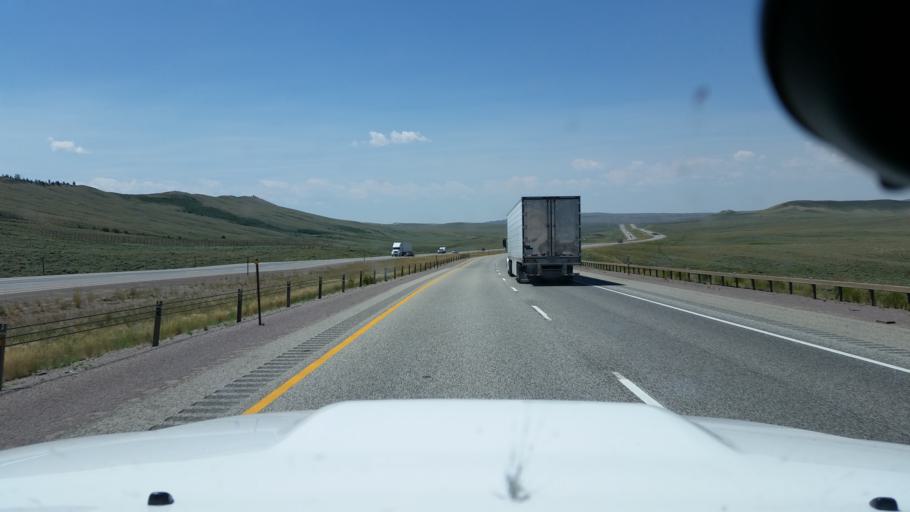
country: US
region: Wyoming
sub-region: Carbon County
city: Saratoga
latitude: 41.7517
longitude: -106.5233
